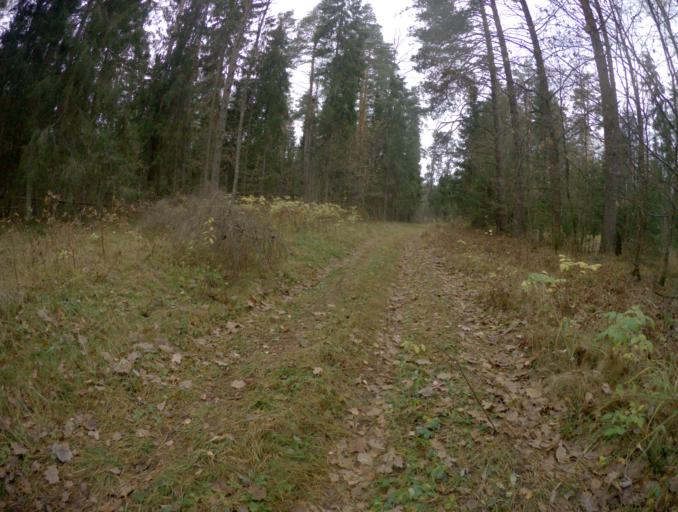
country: RU
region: Vladimir
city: Orgtrud
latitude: 56.1133
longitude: 40.6196
